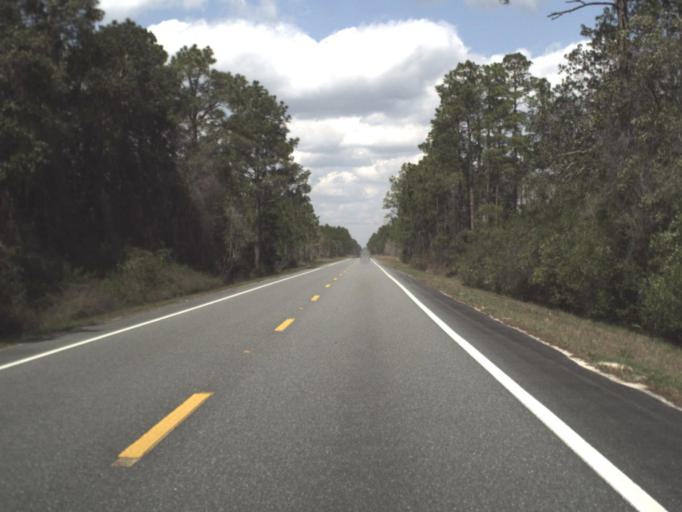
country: US
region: Florida
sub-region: Gulf County
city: Wewahitchka
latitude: 29.9938
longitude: -84.9768
